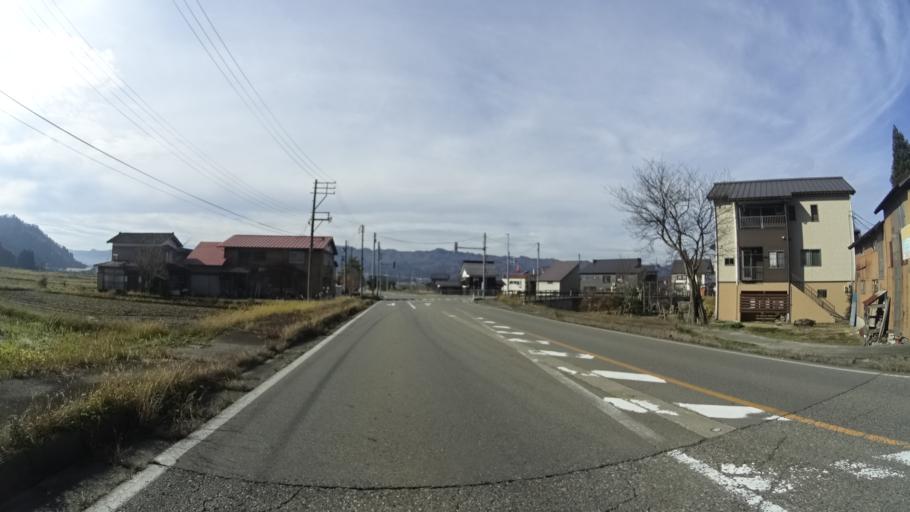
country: JP
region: Niigata
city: Muikamachi
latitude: 37.1289
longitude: 138.9405
